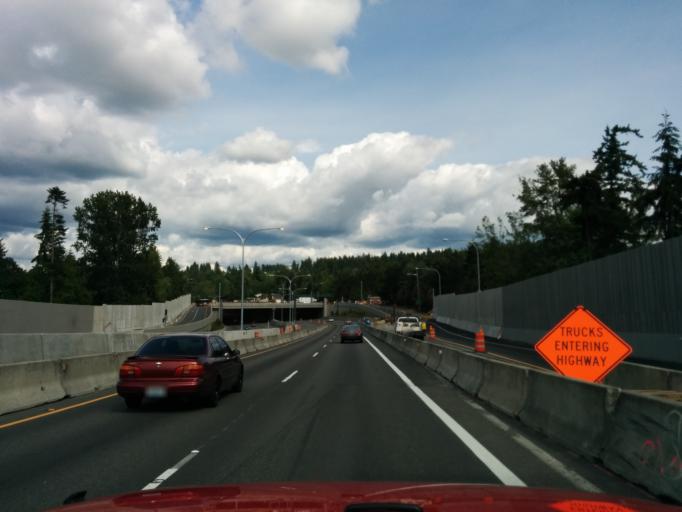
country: US
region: Washington
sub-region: King County
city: Clyde Hill
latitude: 47.6361
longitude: -122.2321
